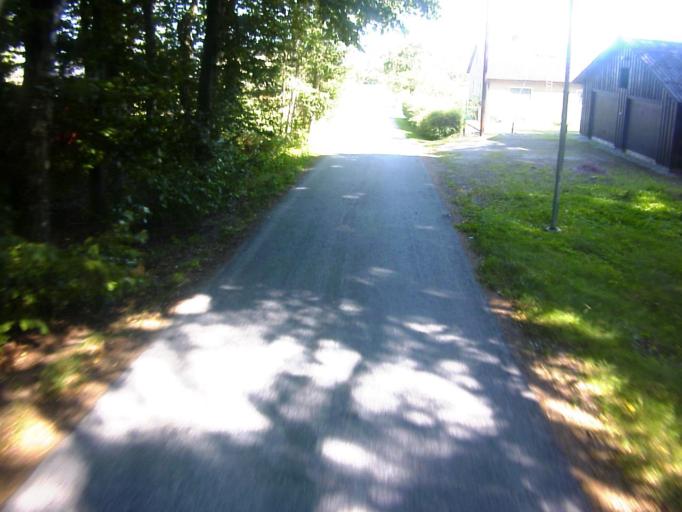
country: SE
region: Blekinge
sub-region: Solvesborgs Kommun
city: Soelvesborg
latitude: 56.0986
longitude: 14.6150
